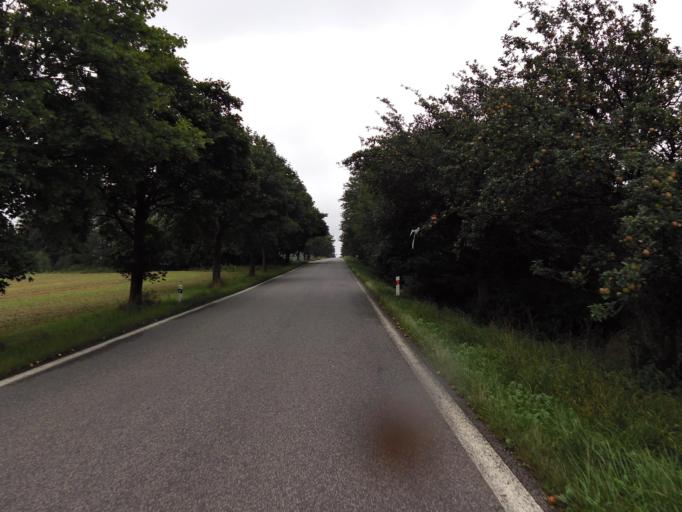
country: CZ
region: Jihocesky
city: Mlada Vozice
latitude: 49.4718
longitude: 14.7792
